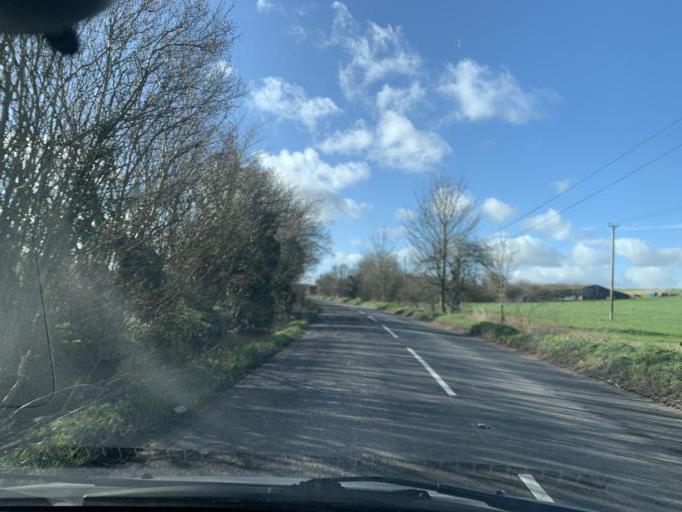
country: GB
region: England
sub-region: Wiltshire
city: Shrewton
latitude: 51.1965
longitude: -1.9144
